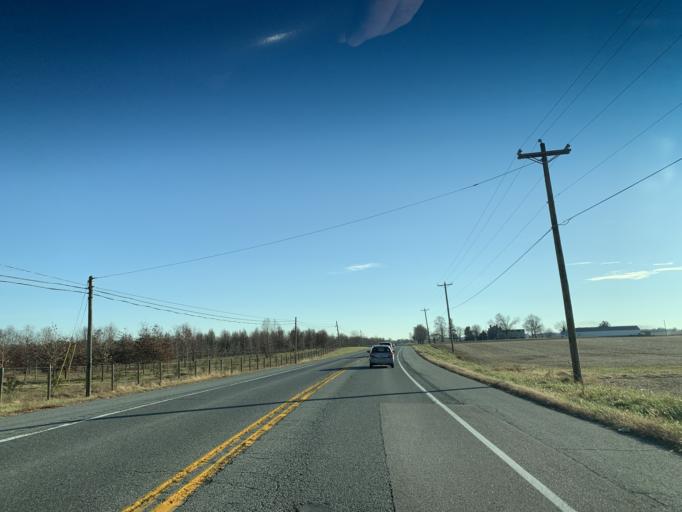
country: US
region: Delaware
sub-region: New Castle County
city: Middletown
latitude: 39.4271
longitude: -75.8605
